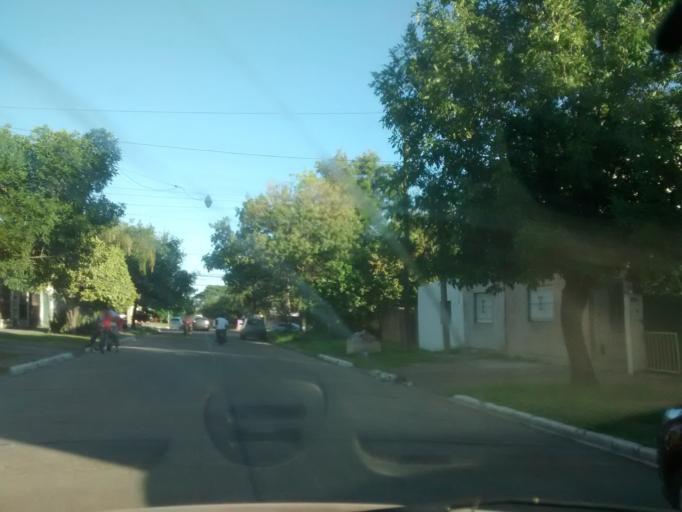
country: AR
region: Chaco
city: Resistencia
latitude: -27.4632
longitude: -58.9924
